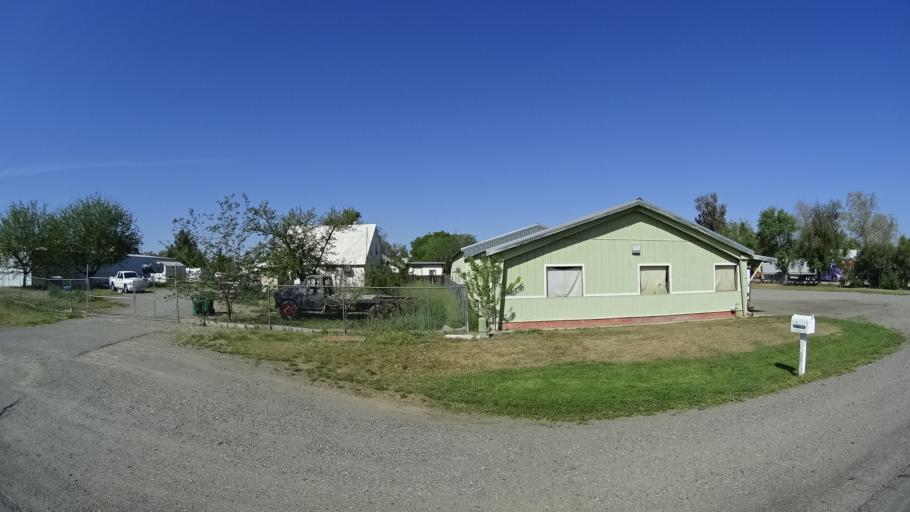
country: US
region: California
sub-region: Glenn County
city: Willows
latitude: 39.5319
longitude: -122.1935
